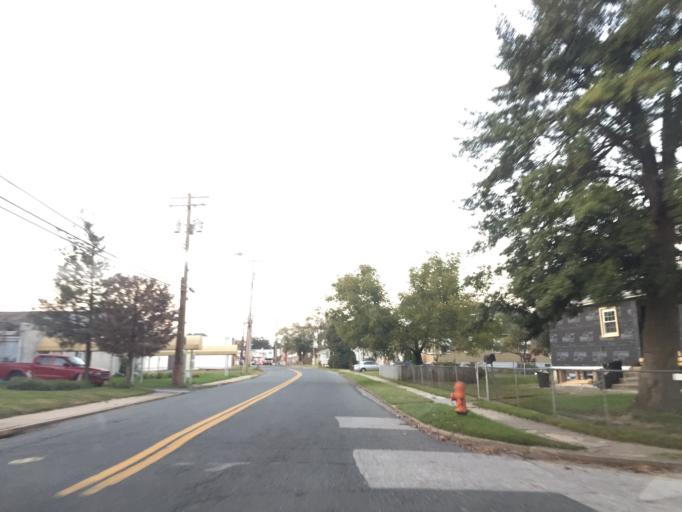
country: US
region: Maryland
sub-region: Baltimore County
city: Essex
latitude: 39.3050
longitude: -76.4787
